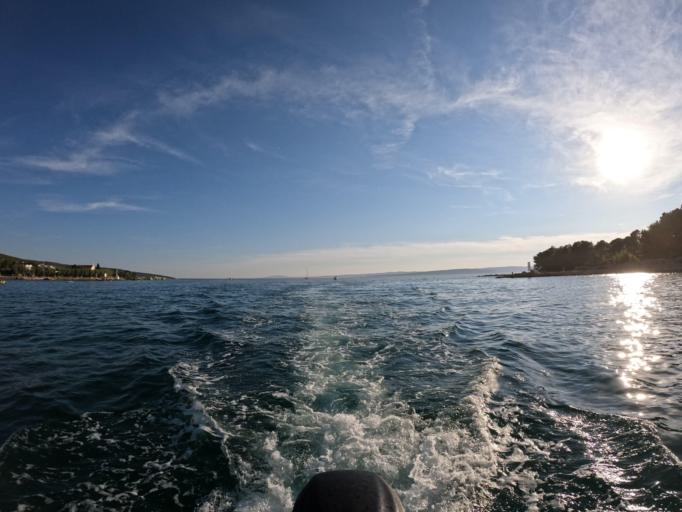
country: HR
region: Primorsko-Goranska
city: Punat
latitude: 45.0144
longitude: 14.6227
